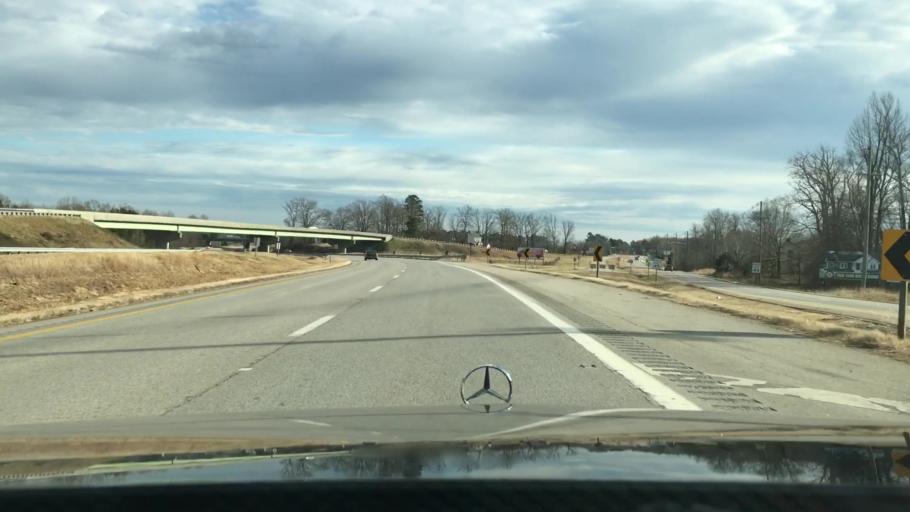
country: US
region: Virginia
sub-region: Pittsylvania County
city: Mount Hermon
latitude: 36.7031
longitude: -79.3702
